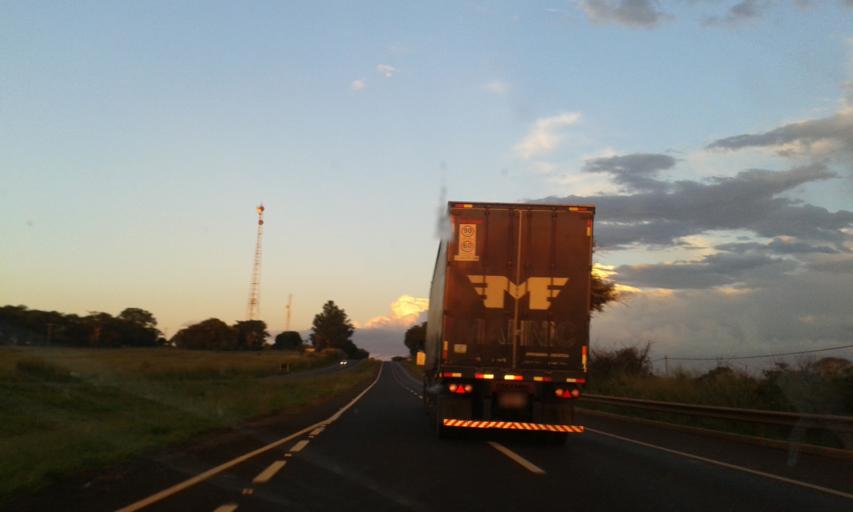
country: BR
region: Minas Gerais
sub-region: Monte Alegre De Minas
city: Monte Alegre de Minas
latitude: -18.8904
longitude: -48.6986
